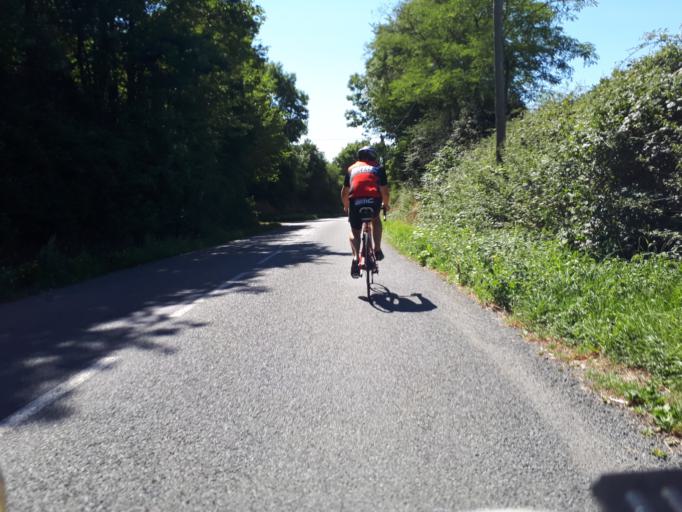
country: FR
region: Rhone-Alpes
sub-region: Departement de la Loire
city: Panissieres
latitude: 45.8010
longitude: 4.3396
